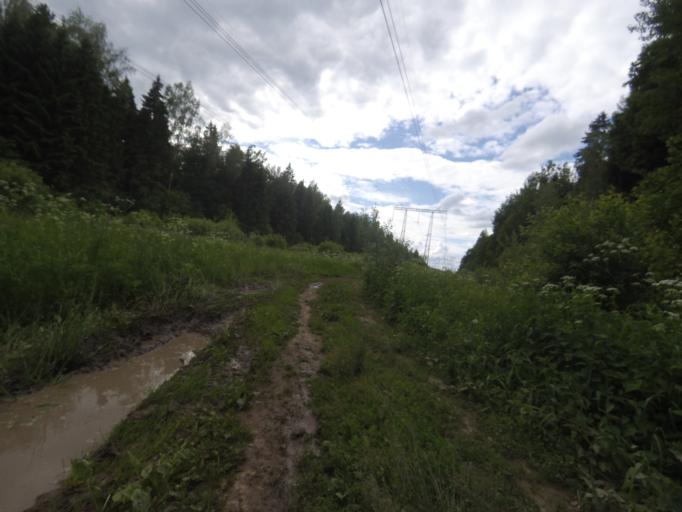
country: RU
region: Moskovskaya
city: Marfino
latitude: 56.0580
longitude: 37.6338
